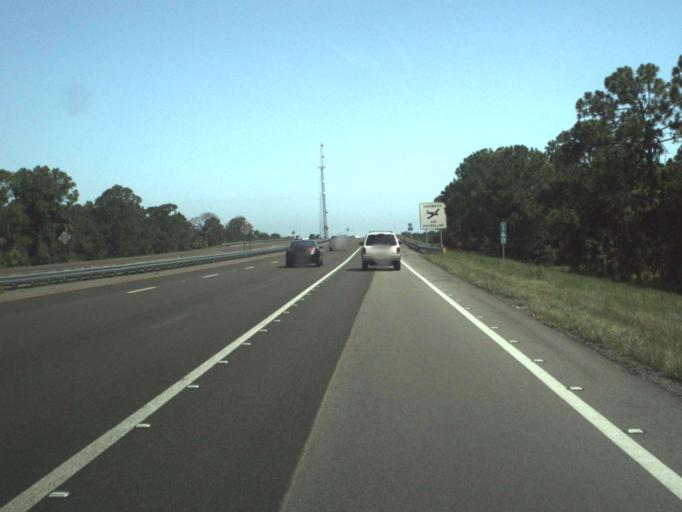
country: US
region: Florida
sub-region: Indian River County
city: Roseland
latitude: 27.8226
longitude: -80.5548
